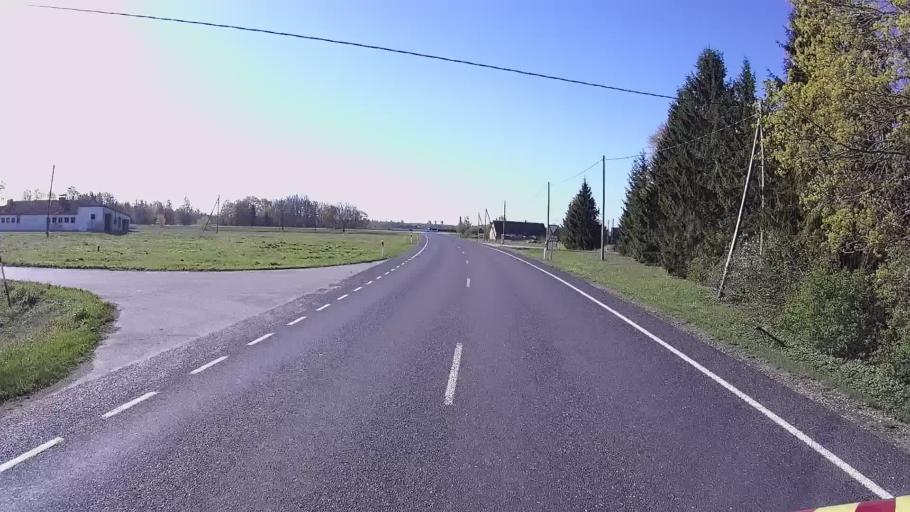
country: EE
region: Viljandimaa
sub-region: Vohma linn
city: Vohma
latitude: 58.6618
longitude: 25.6081
